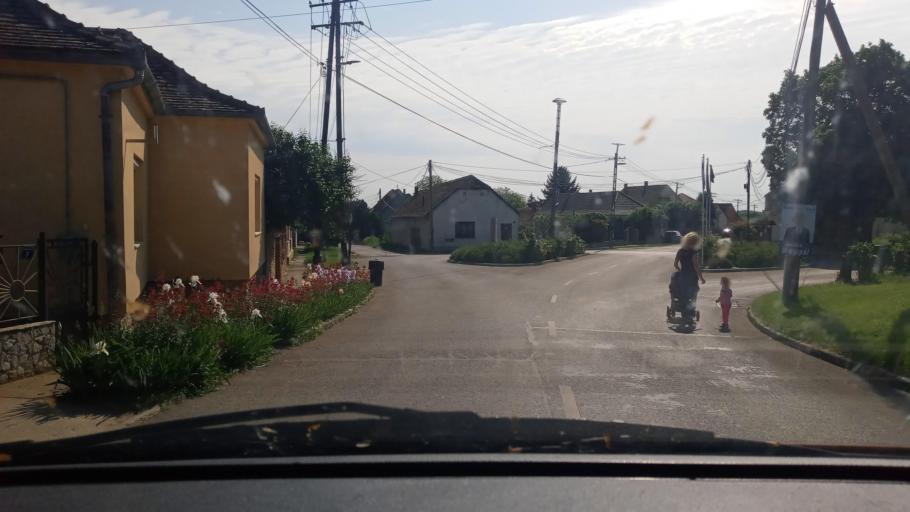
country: HU
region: Baranya
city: Kozarmisleny
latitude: 46.0091
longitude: 18.3280
